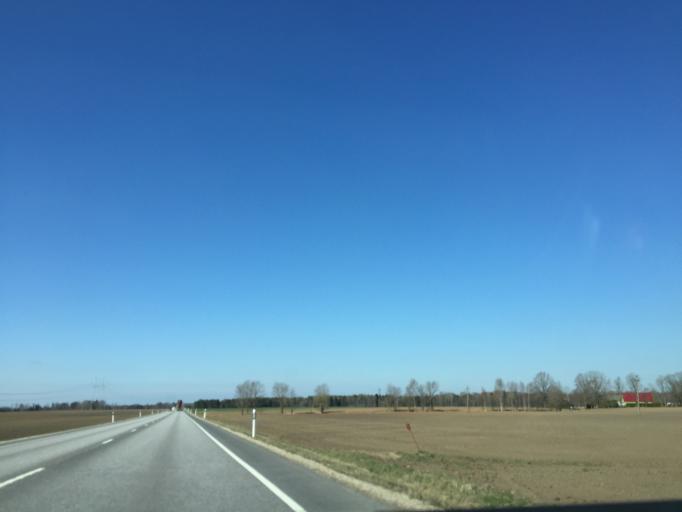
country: EE
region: Tartu
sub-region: Noo vald
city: Noo
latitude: 58.3481
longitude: 26.5071
